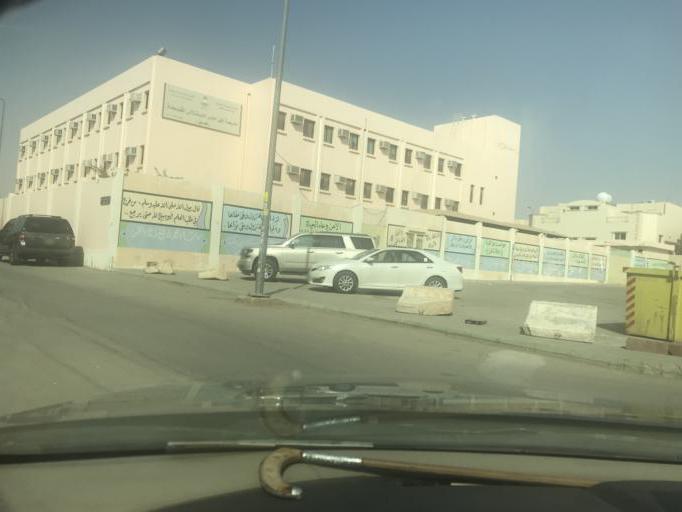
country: SA
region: Ar Riyad
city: Riyadh
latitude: 24.7380
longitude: 46.7785
